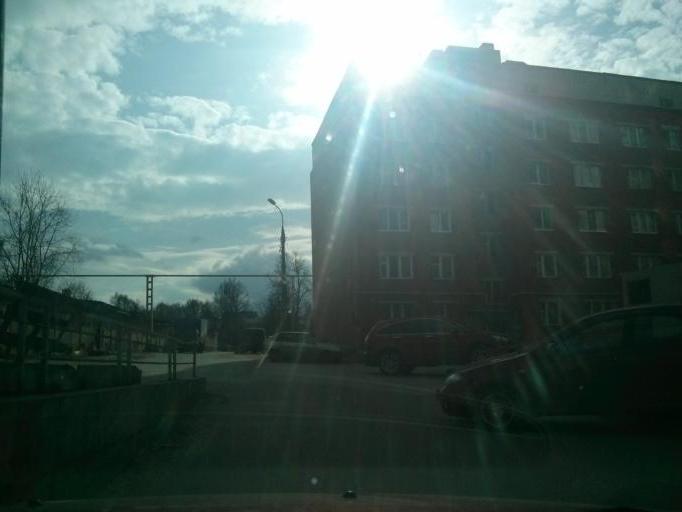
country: RU
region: Nizjnij Novgorod
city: Nizhniy Novgorod
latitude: 56.2659
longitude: 44.0162
